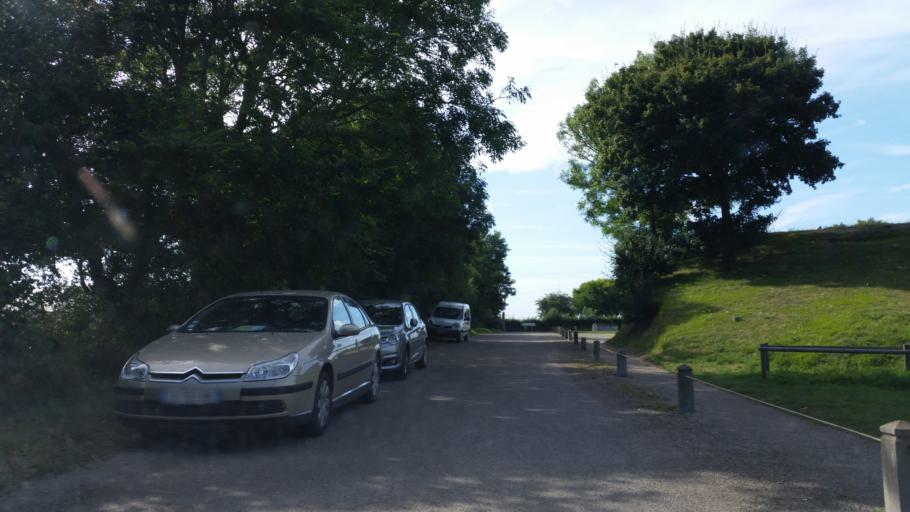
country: FR
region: Lower Normandy
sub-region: Departement de la Manche
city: Sainte-Mere-Eglise
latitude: 49.4604
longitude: -1.3062
